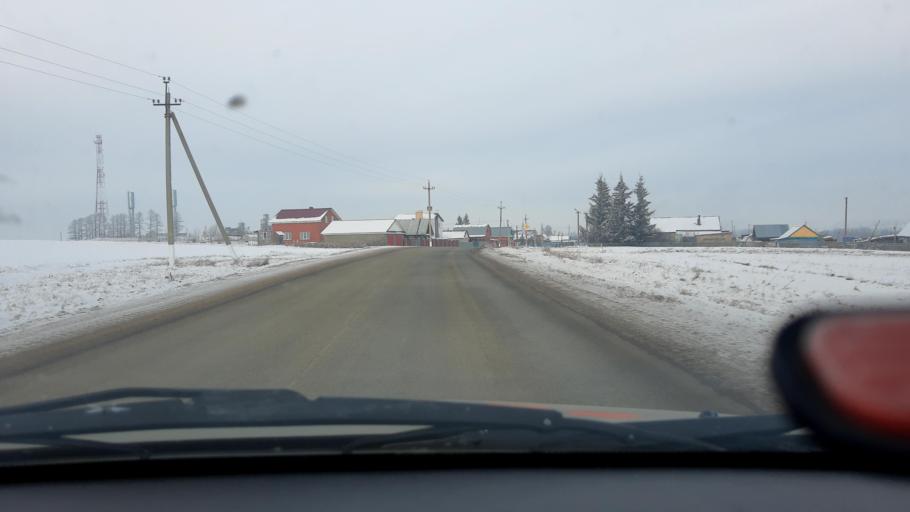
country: RU
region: Bashkortostan
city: Avdon
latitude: 54.4101
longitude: 55.8055
